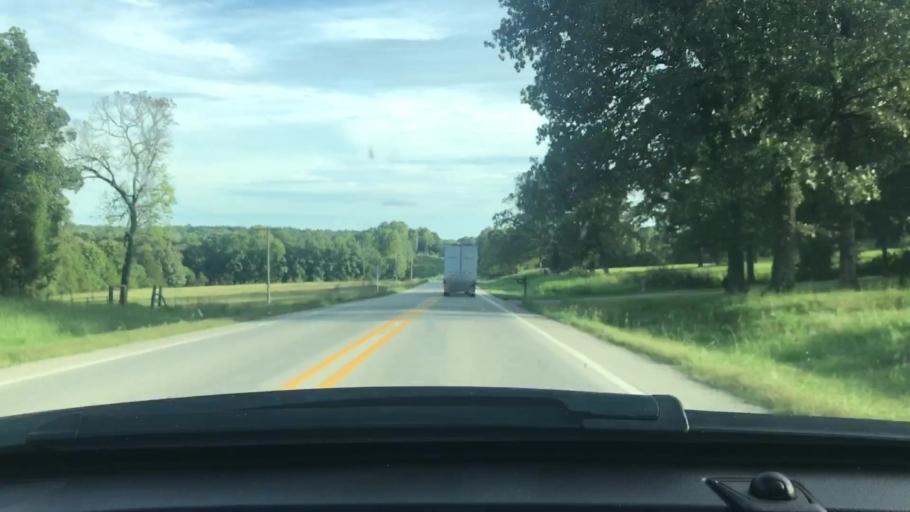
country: US
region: Arkansas
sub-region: Randolph County
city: Pocahontas
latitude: 36.1604
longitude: -91.1621
